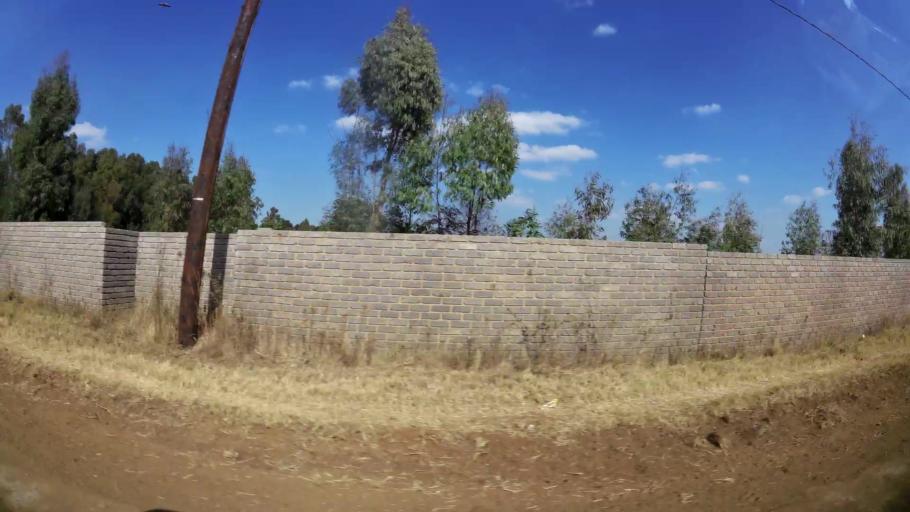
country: ZA
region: Gauteng
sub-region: Ekurhuleni Metropolitan Municipality
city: Benoni
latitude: -26.0804
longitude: 28.3669
